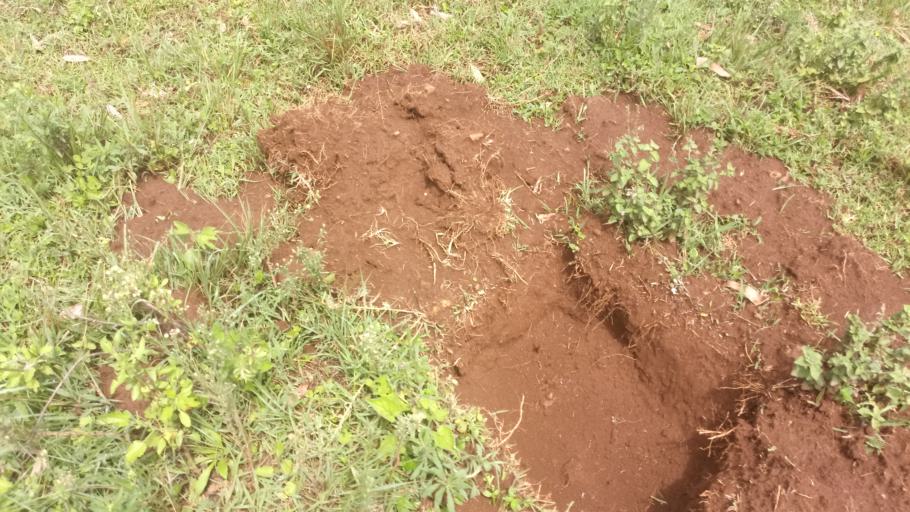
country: KE
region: Kirinyaga
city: Keruguya
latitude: -0.3992
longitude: 37.1580
